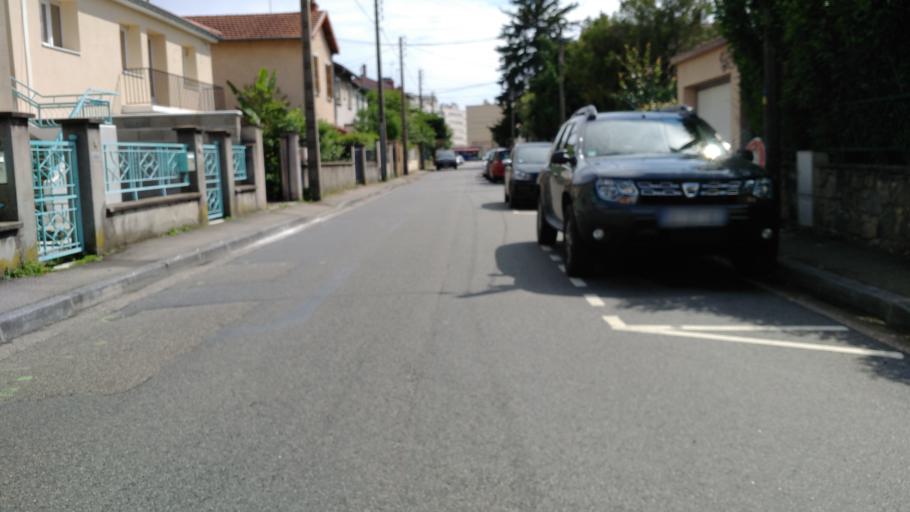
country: FR
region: Rhone-Alpes
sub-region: Departement du Rhone
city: Venissieux
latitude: 45.7251
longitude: 4.8847
